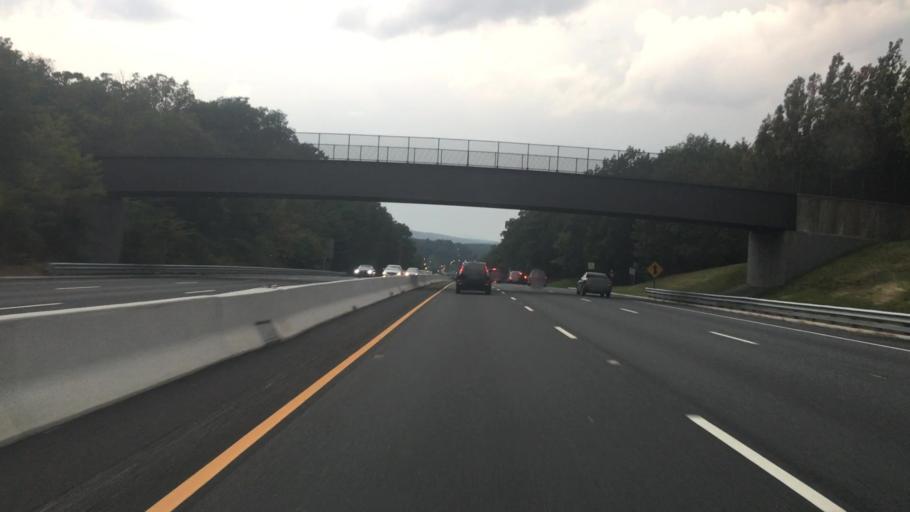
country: US
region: New Jersey
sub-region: Bergen County
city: Franklin Lakes
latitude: 41.0136
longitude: -74.2076
